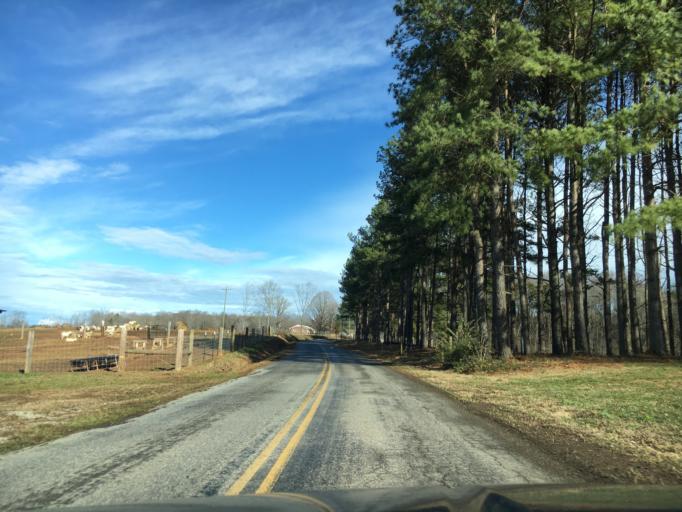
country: US
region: Virginia
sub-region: Amelia County
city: Amelia Court House
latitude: 37.3836
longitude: -78.1248
